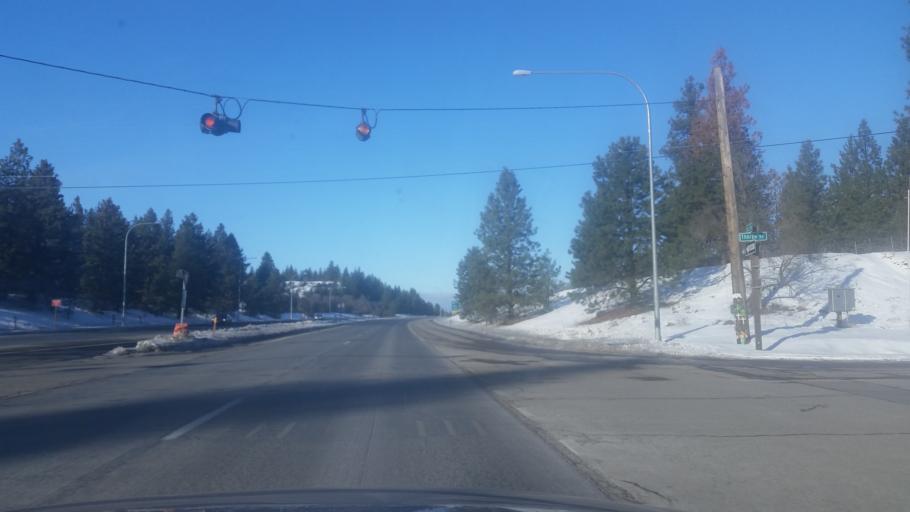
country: US
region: Washington
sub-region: Spokane County
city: Spokane
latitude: 47.6323
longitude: -117.4445
